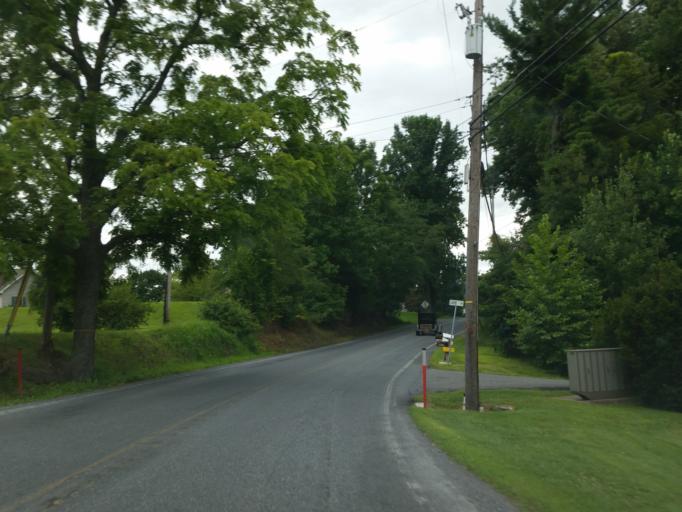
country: US
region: Pennsylvania
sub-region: Berks County
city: Alleghenyville
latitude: 40.2379
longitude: -75.9921
